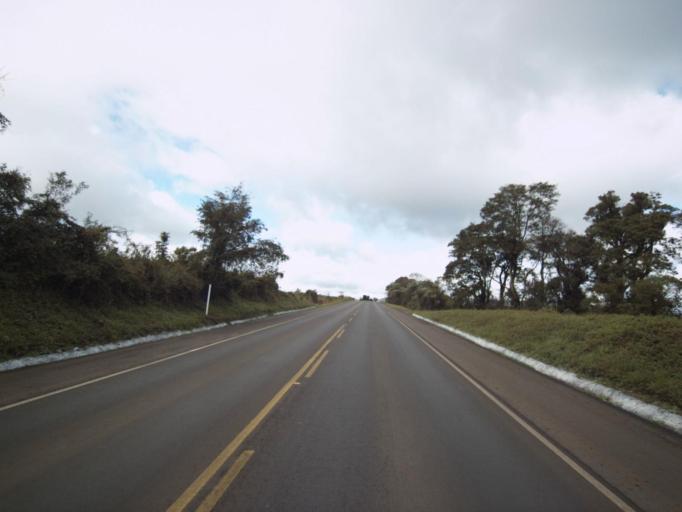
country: BR
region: Santa Catarina
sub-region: Concordia
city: Concordia
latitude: -27.0995
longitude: -51.8999
